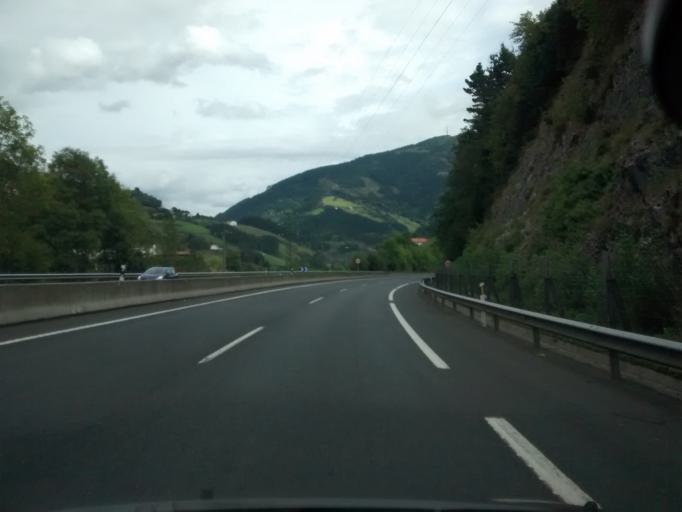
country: ES
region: Basque Country
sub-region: Provincia de Guipuzcoa
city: Eibar
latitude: 43.1887
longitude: -2.4563
